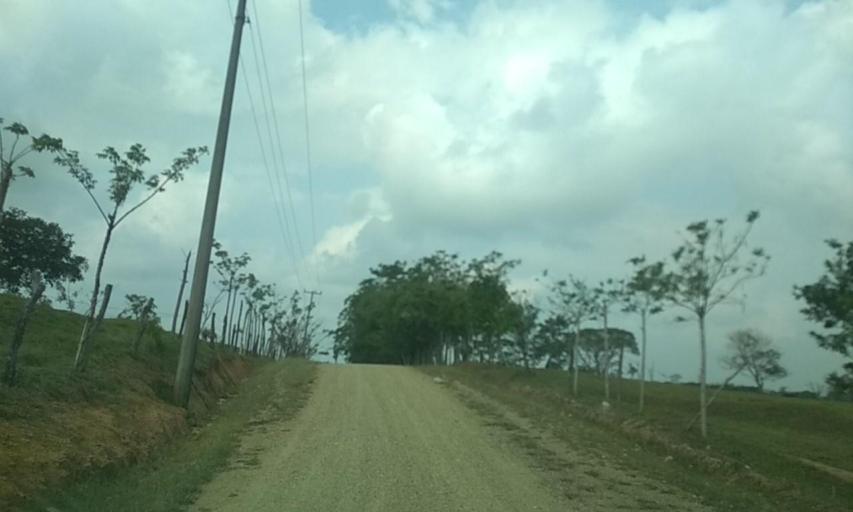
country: MX
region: Tabasco
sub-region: Huimanguillo
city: Francisco Rueda
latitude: 17.6562
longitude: -93.7578
